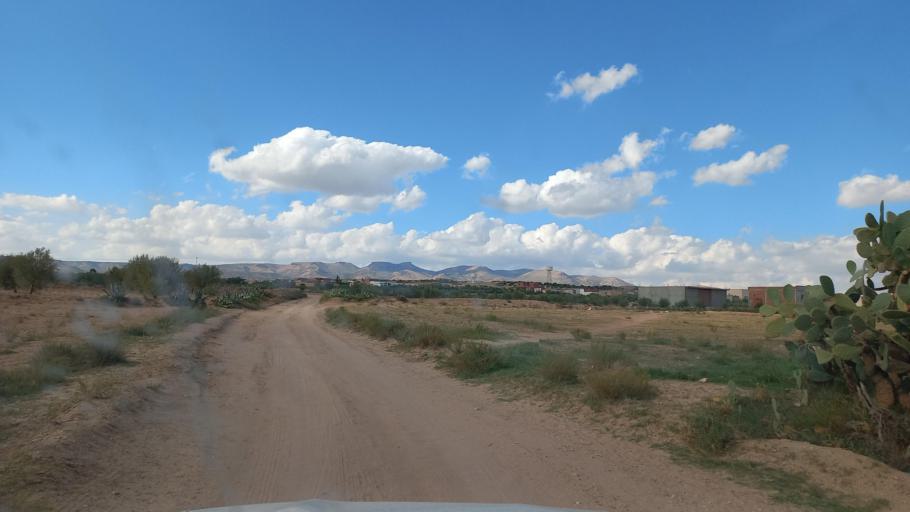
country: TN
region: Al Qasrayn
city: Sbiba
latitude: 35.3840
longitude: 9.0463
